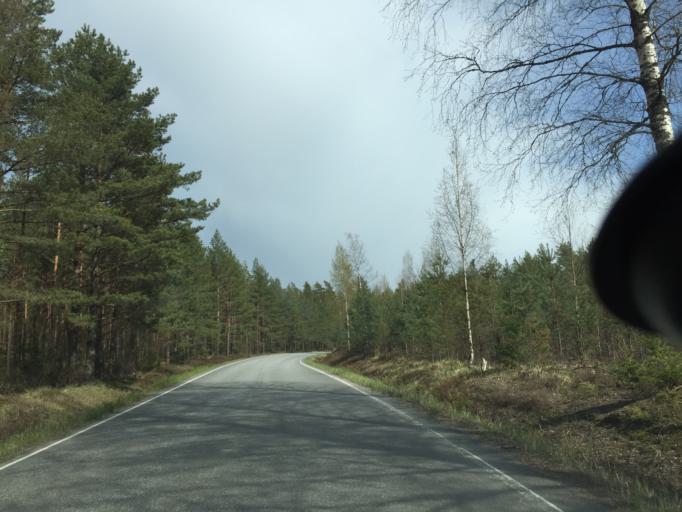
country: FI
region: Uusimaa
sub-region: Raaseporin
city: Hanko
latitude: 59.9727
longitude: 22.9932
